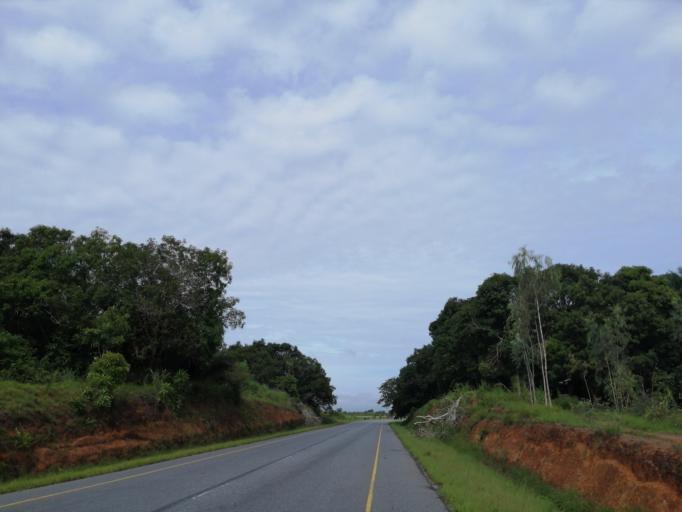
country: SL
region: Northern Province
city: Port Loko
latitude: 8.7707
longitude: -12.8709
